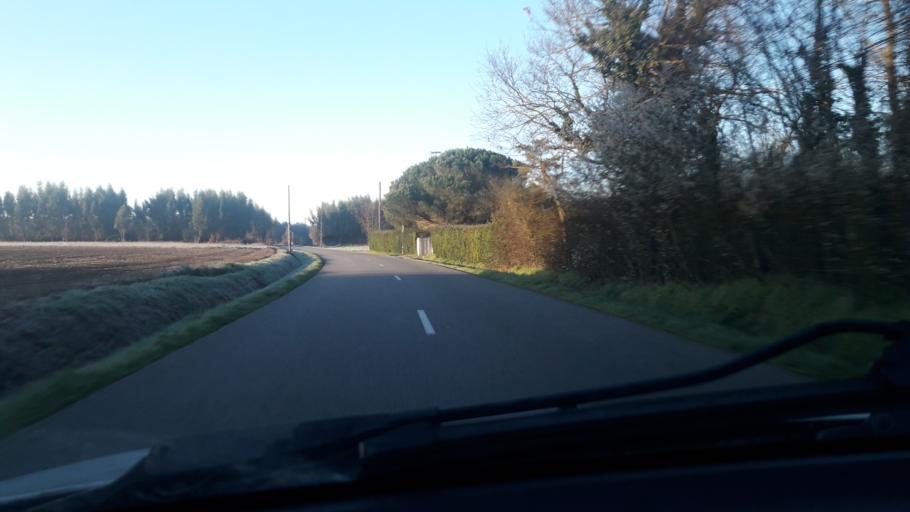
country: FR
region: Midi-Pyrenees
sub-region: Departement de la Haute-Garonne
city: Longages
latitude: 43.3517
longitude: 1.2147
